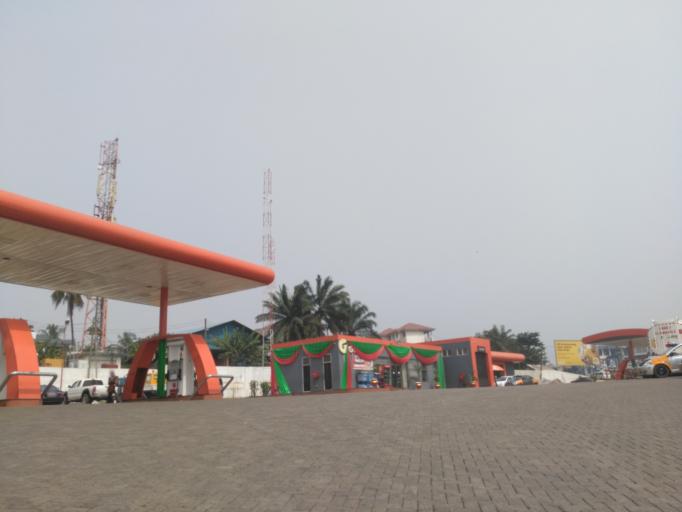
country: GH
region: Ashanti
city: Kumasi
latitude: 6.6729
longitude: -1.6416
